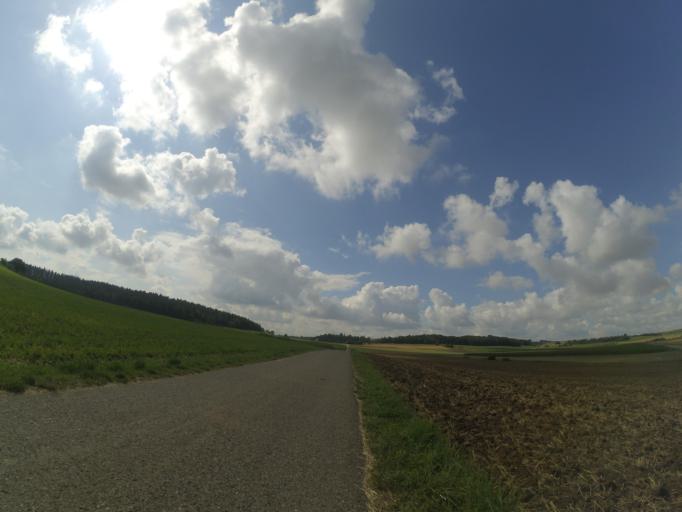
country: DE
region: Baden-Wuerttemberg
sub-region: Tuebingen Region
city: Bernstadt
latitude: 48.4947
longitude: 10.0163
